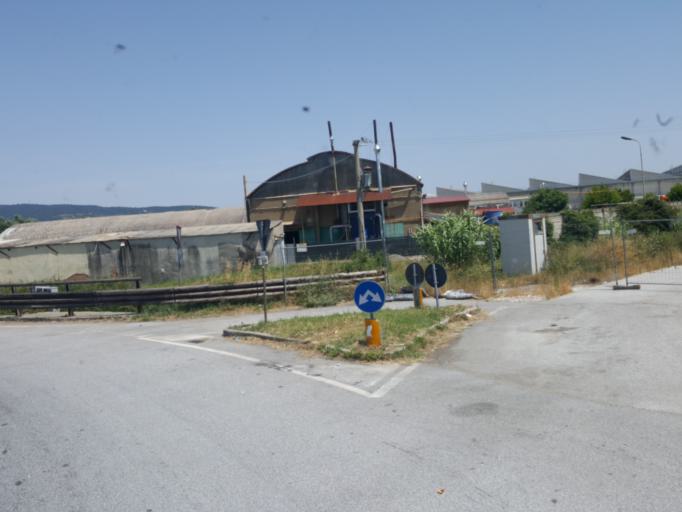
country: IT
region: Tuscany
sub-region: Province of Florence
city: Limite
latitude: 43.7211
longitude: 10.9831
